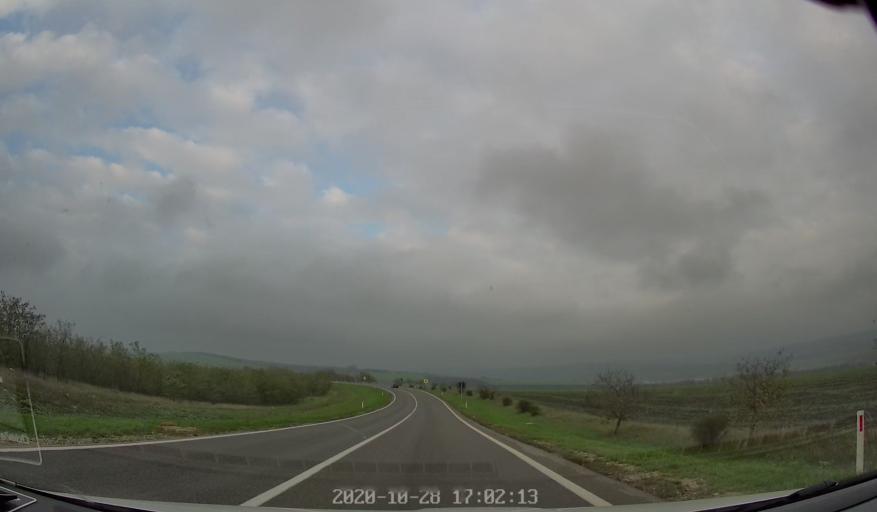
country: MD
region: Gagauzia
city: Bugeac
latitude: 46.4068
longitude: 28.7415
